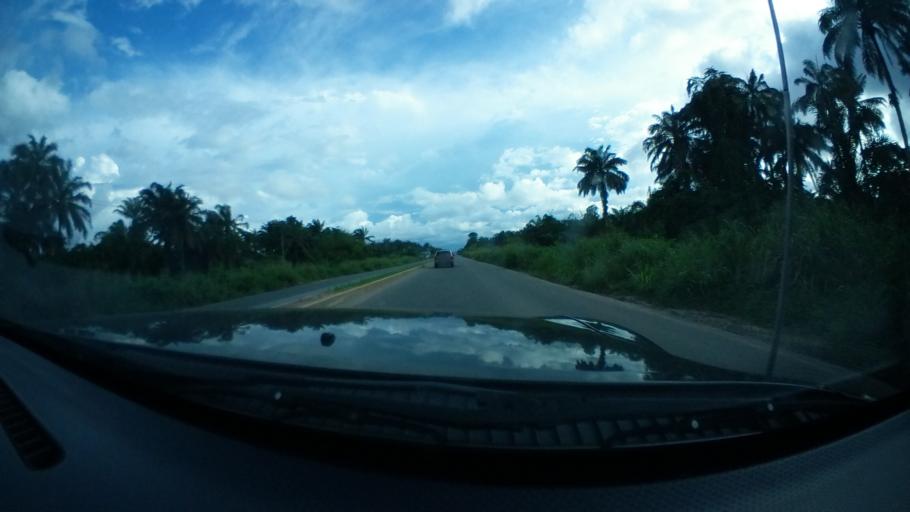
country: NG
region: Imo
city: Orodo
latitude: 5.6215
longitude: 7.0217
